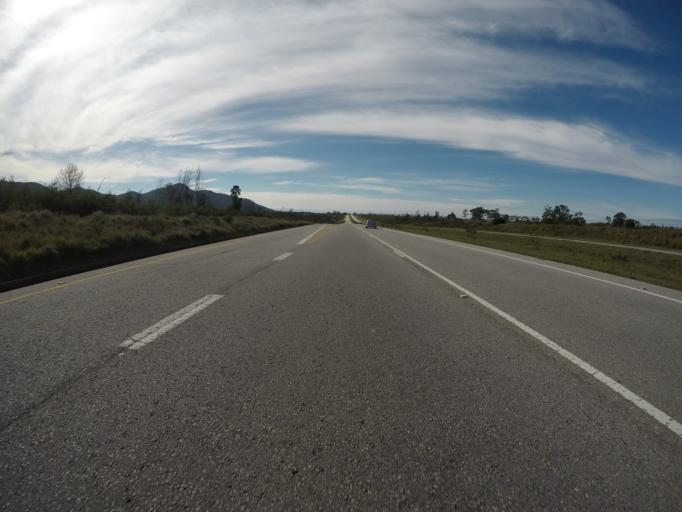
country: ZA
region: Eastern Cape
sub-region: Nelson Mandela Bay Metropolitan Municipality
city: Uitenhage
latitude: -33.9096
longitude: 25.2236
